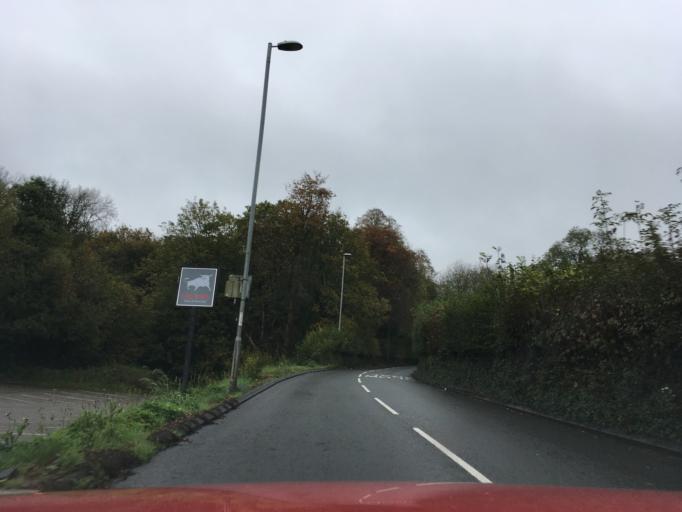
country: GB
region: Wales
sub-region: Newport
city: Caerleon
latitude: 51.6029
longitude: -2.9480
